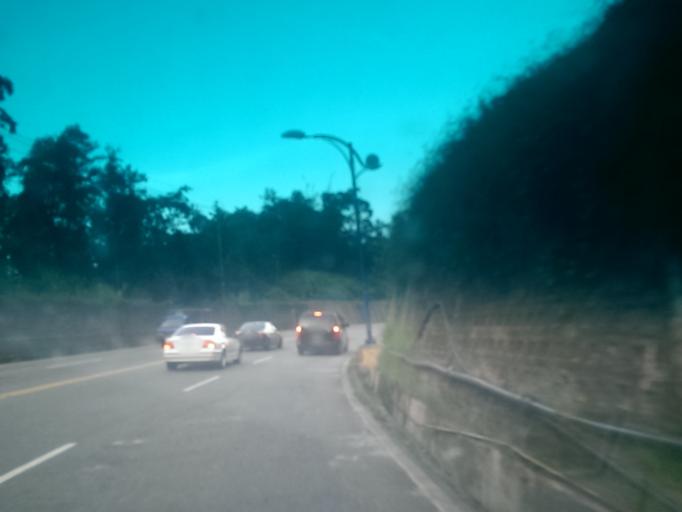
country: TW
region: Taiwan
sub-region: Nantou
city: Puli
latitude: 23.9323
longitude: 120.9222
